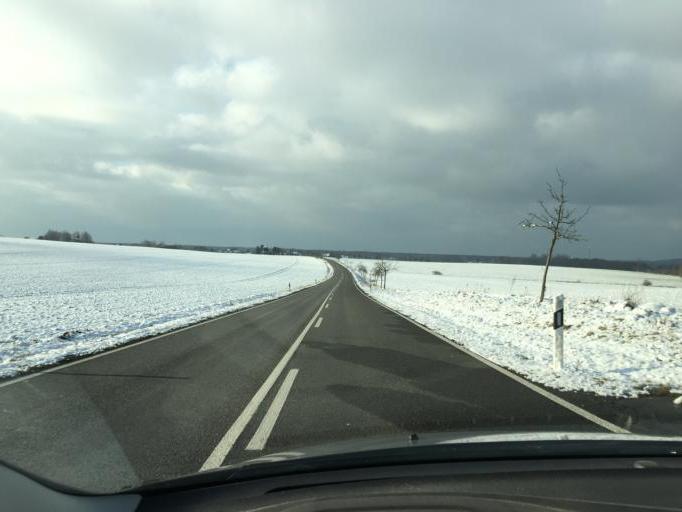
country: DE
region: Saxony
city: Naunhof
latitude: 51.2746
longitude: 12.6588
